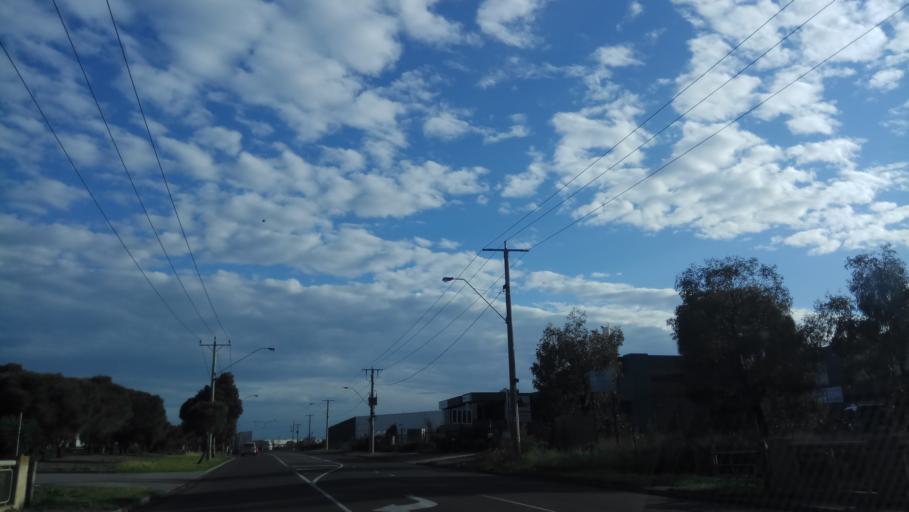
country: AU
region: Victoria
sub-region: Hobsons Bay
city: Laverton
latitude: -37.8480
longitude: 144.7901
